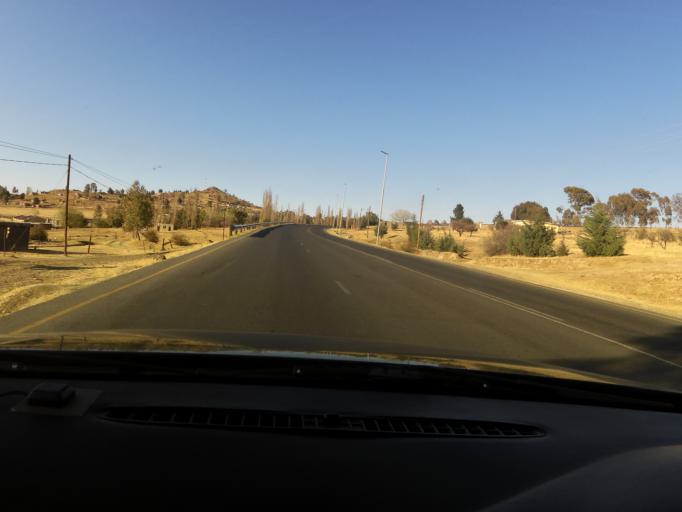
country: LS
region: Mafeteng
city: Mafeteng
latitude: -29.6938
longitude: 27.4355
